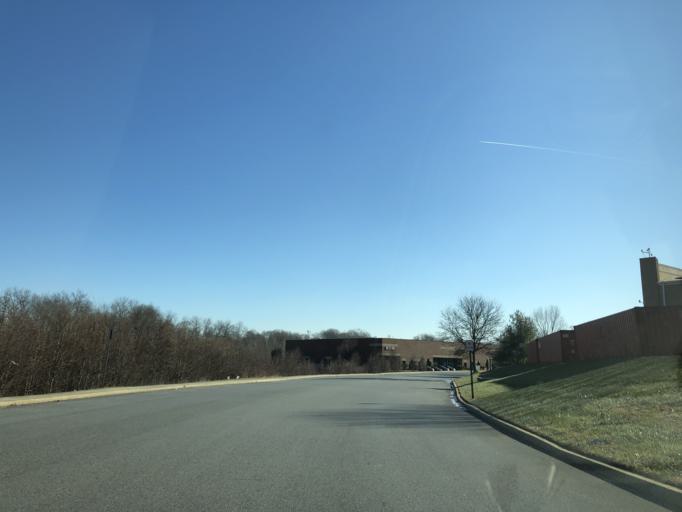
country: US
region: Pennsylvania
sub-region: Delaware County
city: Boothwyn
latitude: 39.8530
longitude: -75.4486
